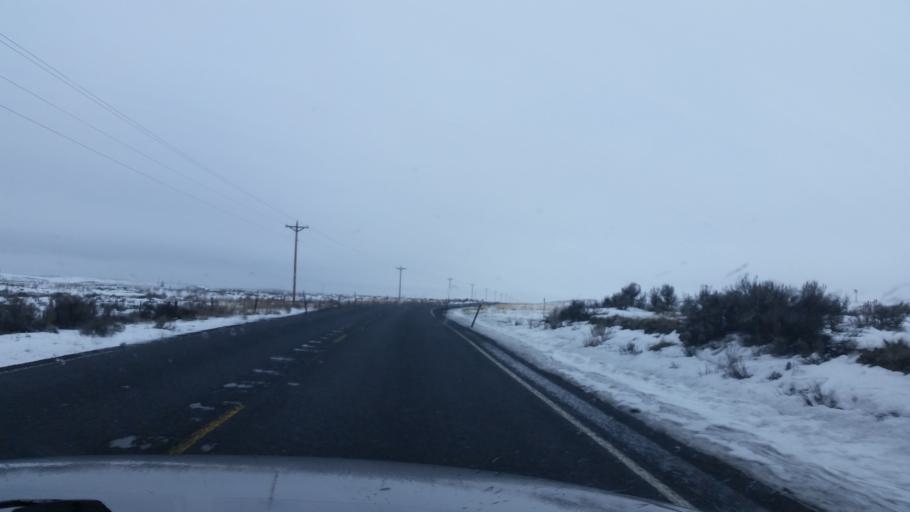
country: US
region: Washington
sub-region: Lincoln County
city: Davenport
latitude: 47.5361
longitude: -118.2888
